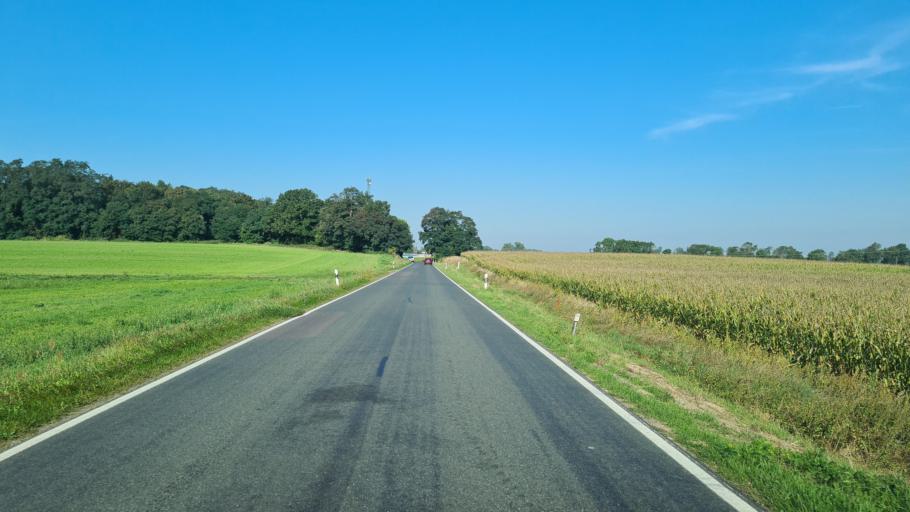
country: DE
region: Brandenburg
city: Friesack
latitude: 52.7355
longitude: 12.6009
